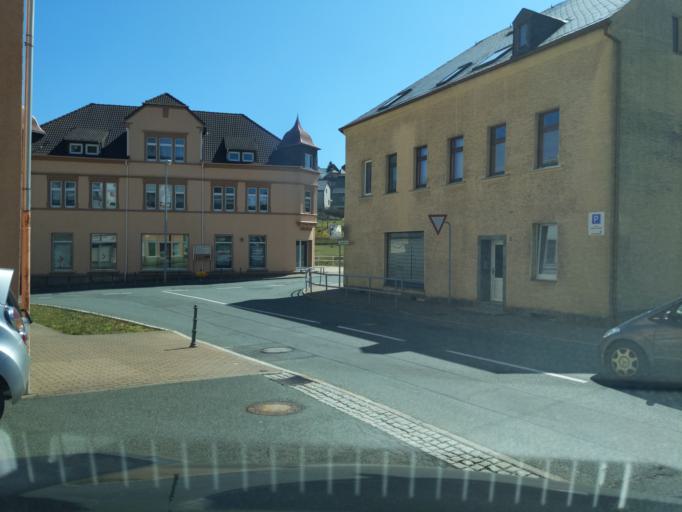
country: DE
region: Saxony
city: Schoenheide
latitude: 50.5059
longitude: 12.5409
